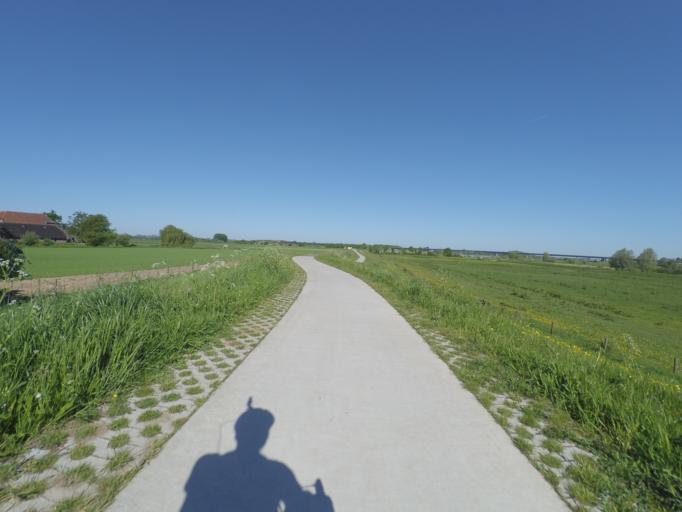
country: NL
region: Gelderland
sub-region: Gemeente Zutphen
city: Zutphen
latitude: 52.1106
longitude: 6.1919
